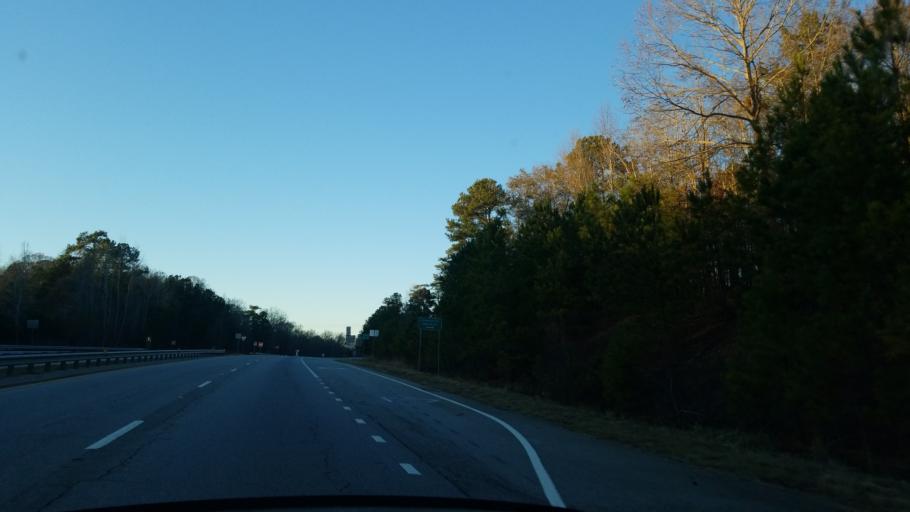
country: US
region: Georgia
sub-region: Chattahoochee County
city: Cusseta
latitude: 32.3129
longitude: -84.7980
